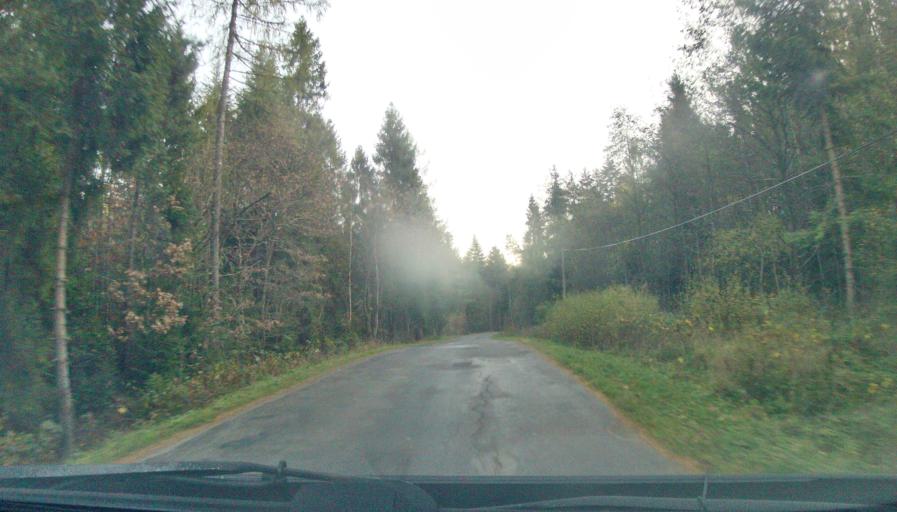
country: PL
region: Lesser Poland Voivodeship
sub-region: Powiat suski
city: Krzeszow
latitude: 49.7604
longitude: 19.4580
